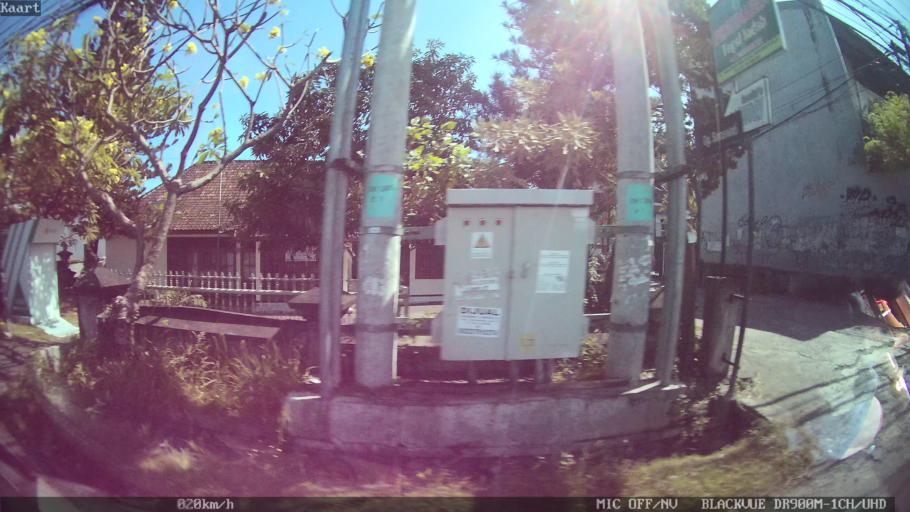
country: ID
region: Bali
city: Denpasar
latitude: -8.6690
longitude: 115.1823
